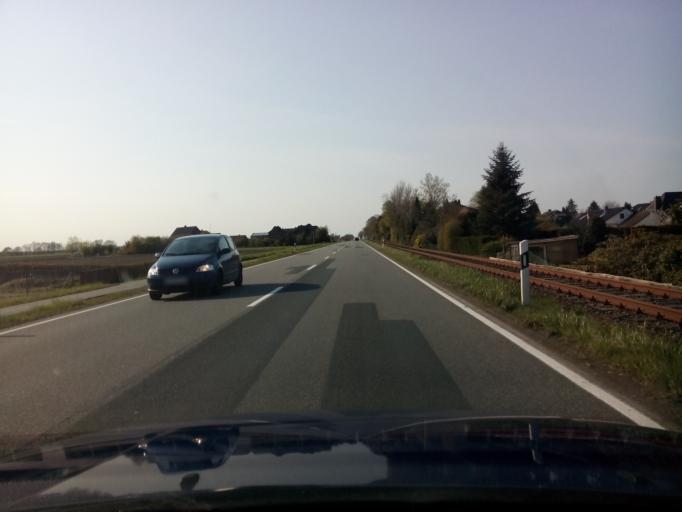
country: DE
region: Lower Saxony
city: Syke
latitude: 52.9002
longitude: 8.8442
